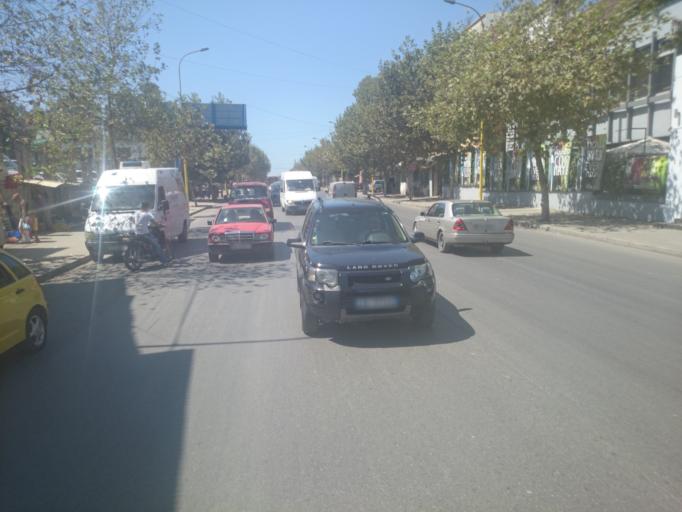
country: AL
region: Tirane
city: Tirana
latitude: 41.3210
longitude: 19.7874
